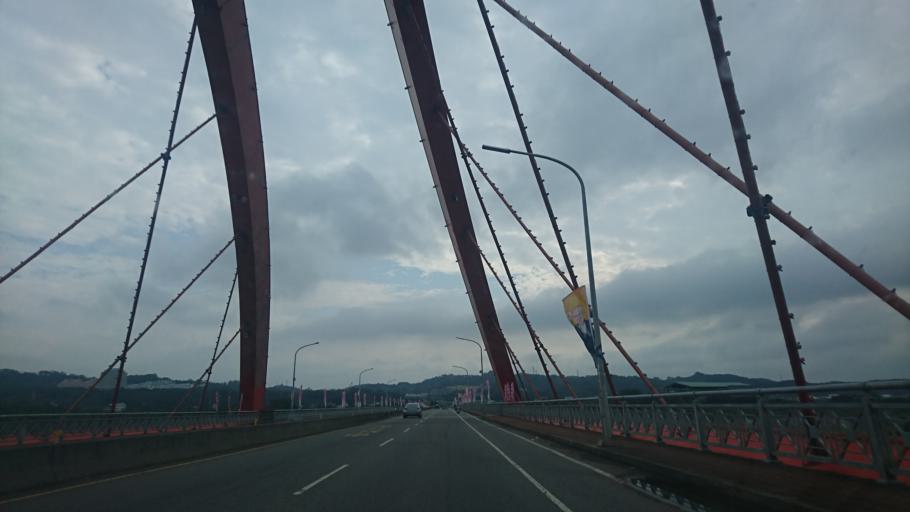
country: TW
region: Taiwan
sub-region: Hsinchu
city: Hsinchu
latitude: 24.6832
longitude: 120.9168
